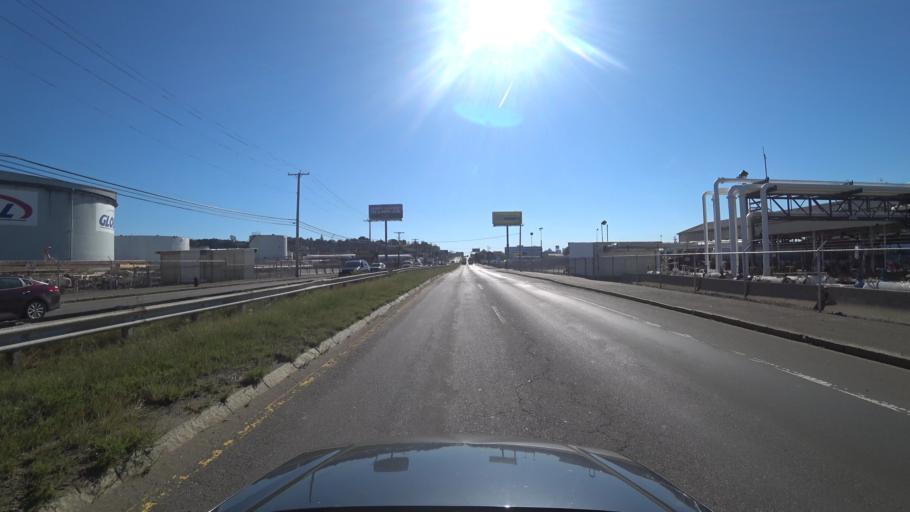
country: US
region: Massachusetts
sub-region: Suffolk County
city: Revere
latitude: 42.3989
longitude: -71.0072
